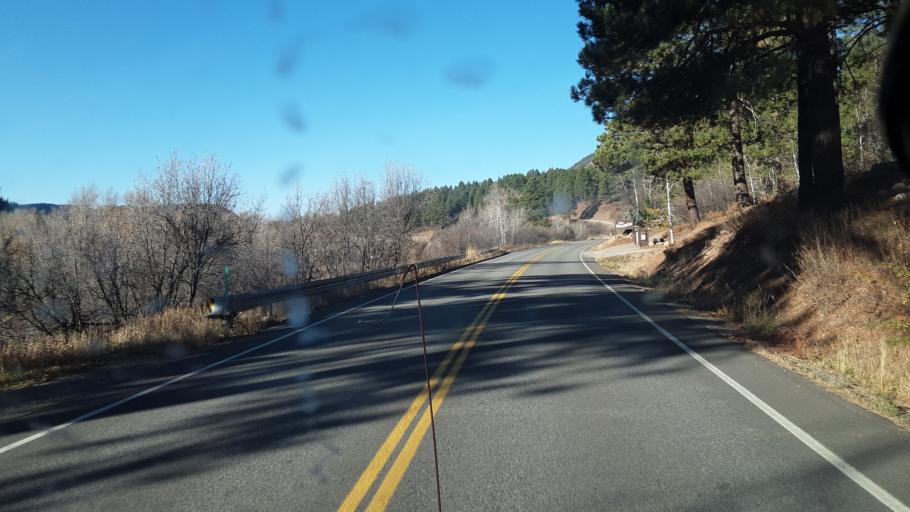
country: US
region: Colorado
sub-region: La Plata County
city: Bayfield
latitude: 37.3538
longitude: -107.6838
